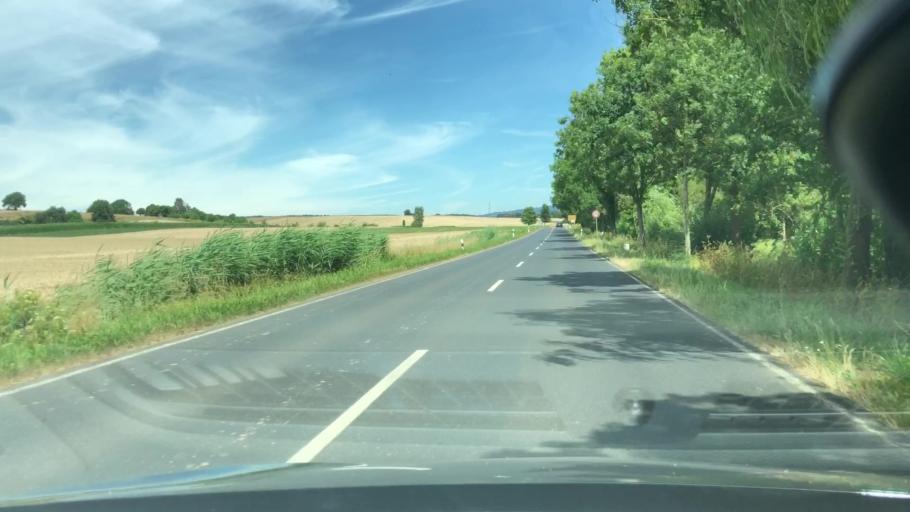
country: DE
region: Hesse
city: Hain-Grundau
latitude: 50.2119
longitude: 9.0953
